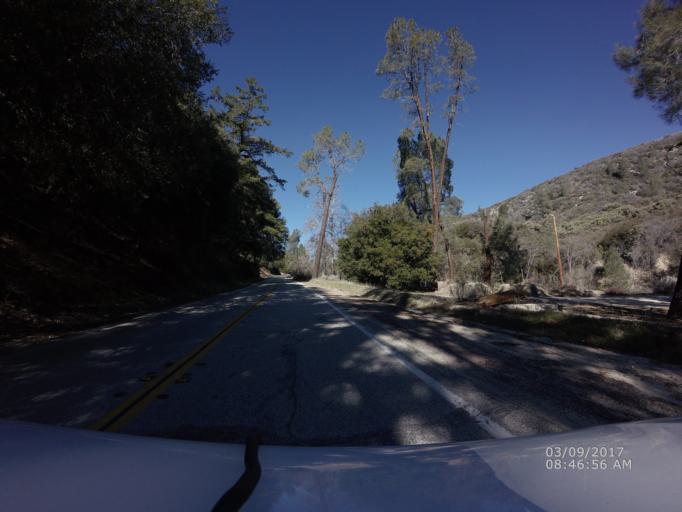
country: US
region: California
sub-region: Los Angeles County
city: Green Valley
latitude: 34.6986
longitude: -118.5077
